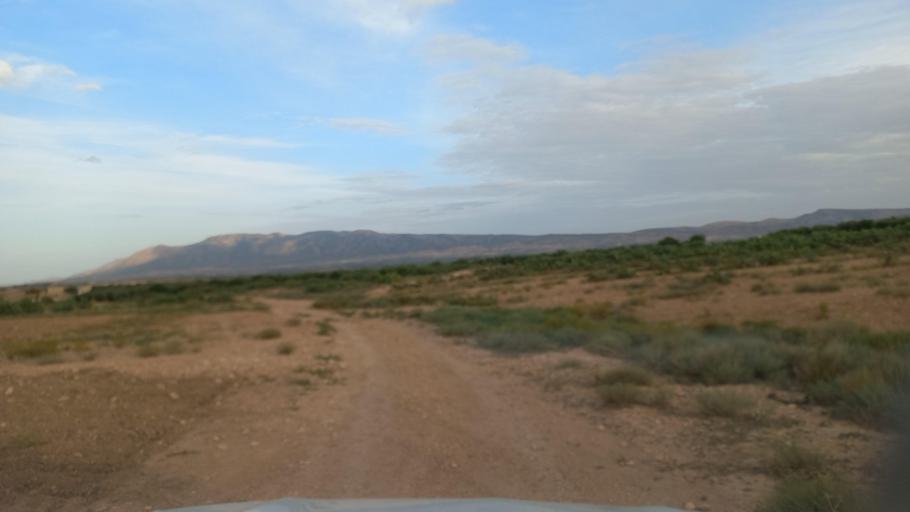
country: TN
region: Al Qasrayn
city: Sbiba
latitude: 35.4393
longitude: 9.0894
